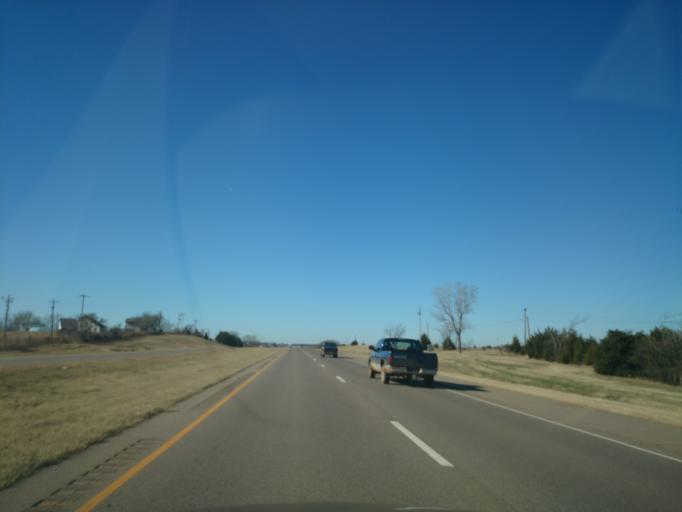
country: US
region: Oklahoma
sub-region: Payne County
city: Stillwater
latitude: 36.1161
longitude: -97.1439
